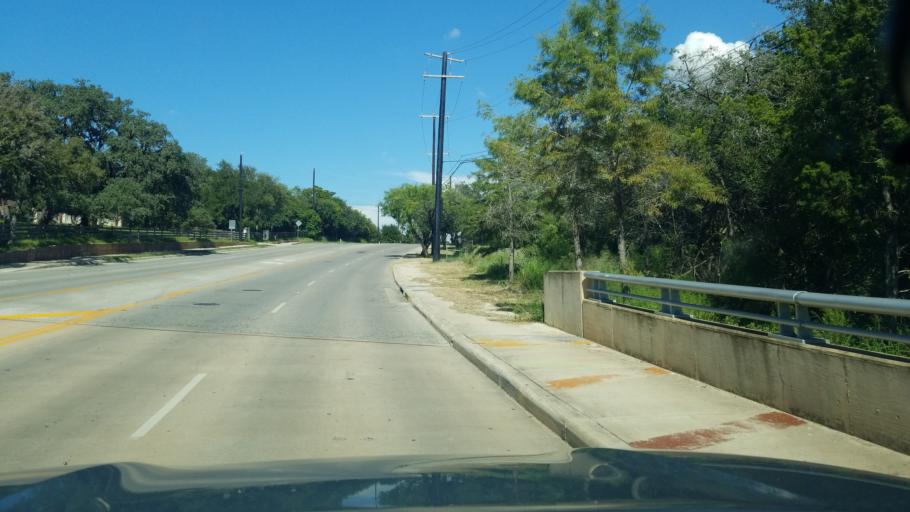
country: US
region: Texas
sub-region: Bexar County
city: Hollywood Park
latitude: 29.5928
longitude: -98.4379
